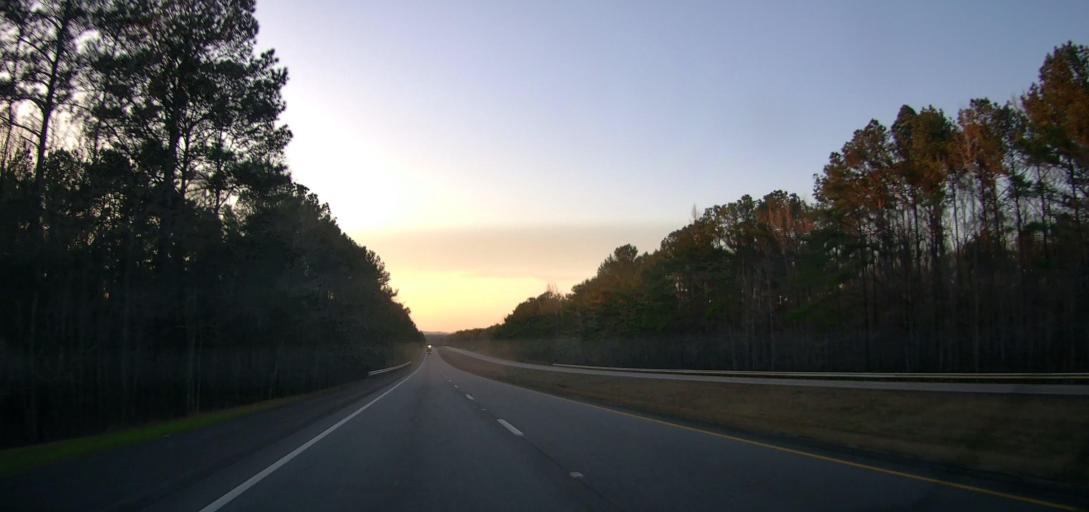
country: US
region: Alabama
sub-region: Coosa County
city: Goodwater
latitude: 33.0239
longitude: -86.1081
